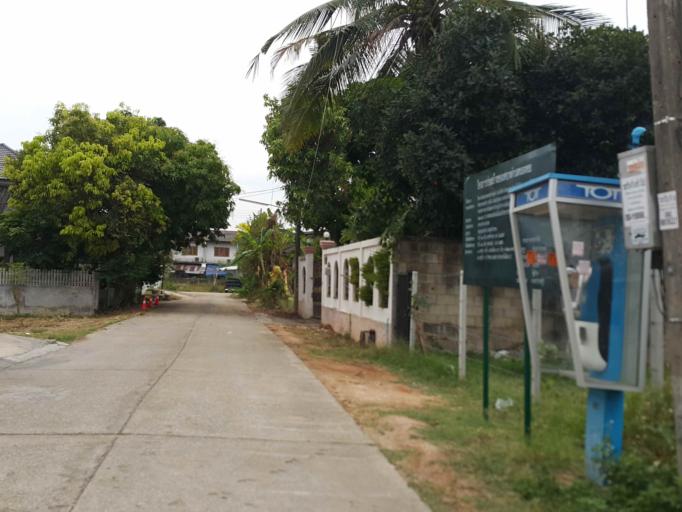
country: TH
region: Chiang Mai
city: Saraphi
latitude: 18.7530
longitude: 99.0186
